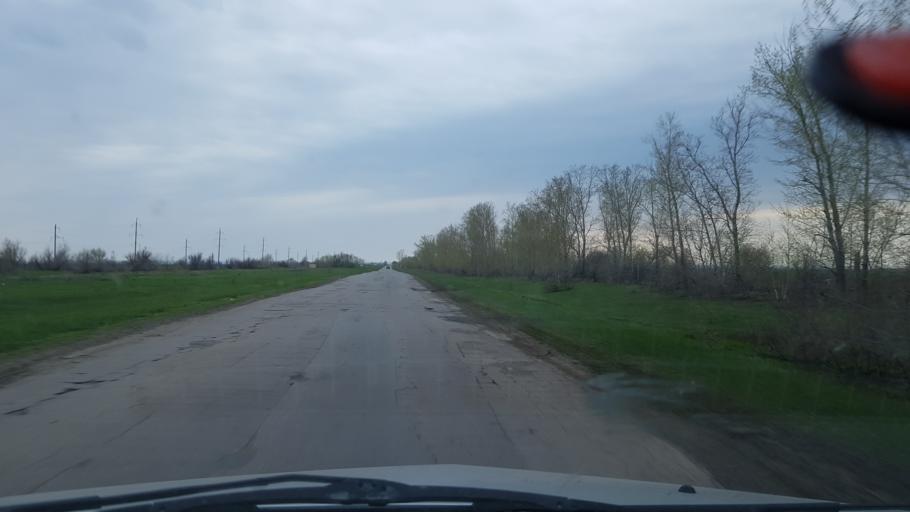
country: RU
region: Samara
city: Podstepki
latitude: 53.6680
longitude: 49.1438
